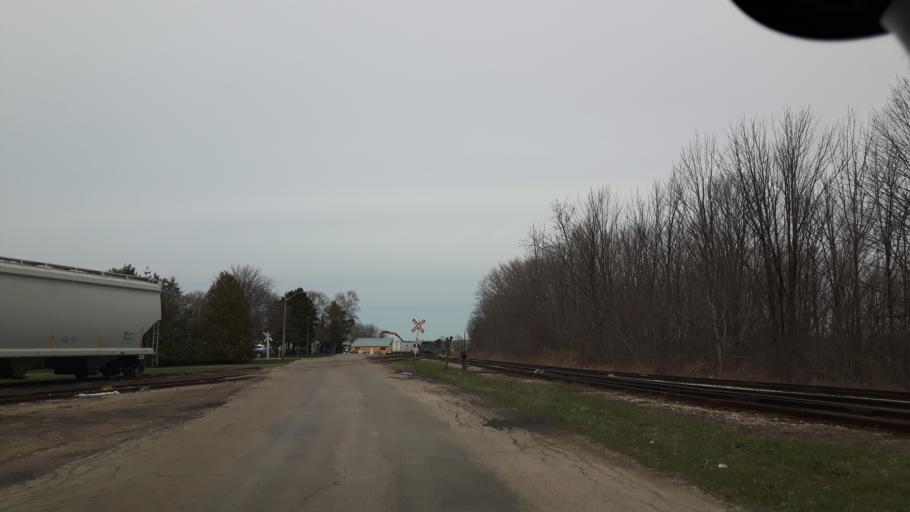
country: CA
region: Ontario
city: Goderich
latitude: 43.7437
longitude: -81.7003
